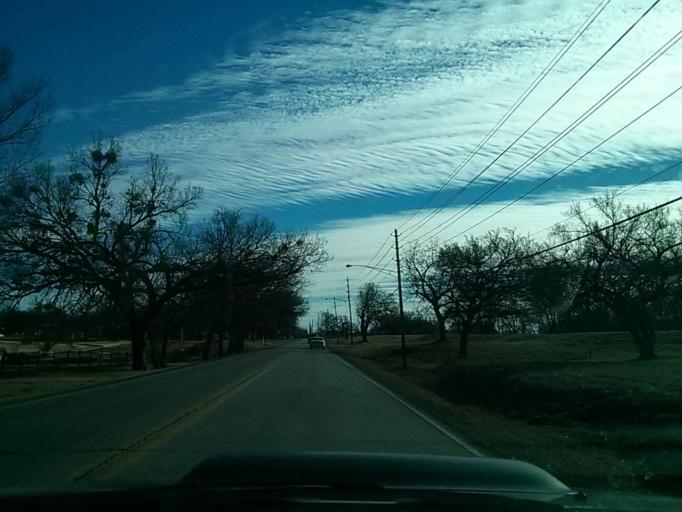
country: US
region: Oklahoma
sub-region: Tulsa County
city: Jenks
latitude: 36.0243
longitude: -95.9905
